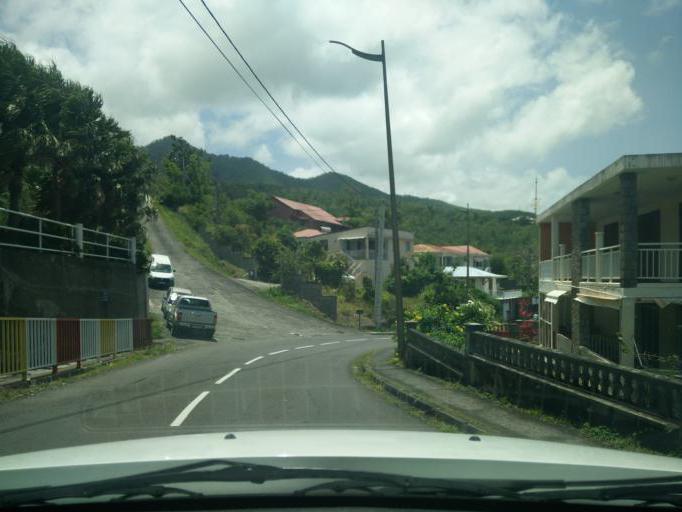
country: GP
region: Guadeloupe
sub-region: Guadeloupe
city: Gourbeyre
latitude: 15.9491
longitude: -61.7010
